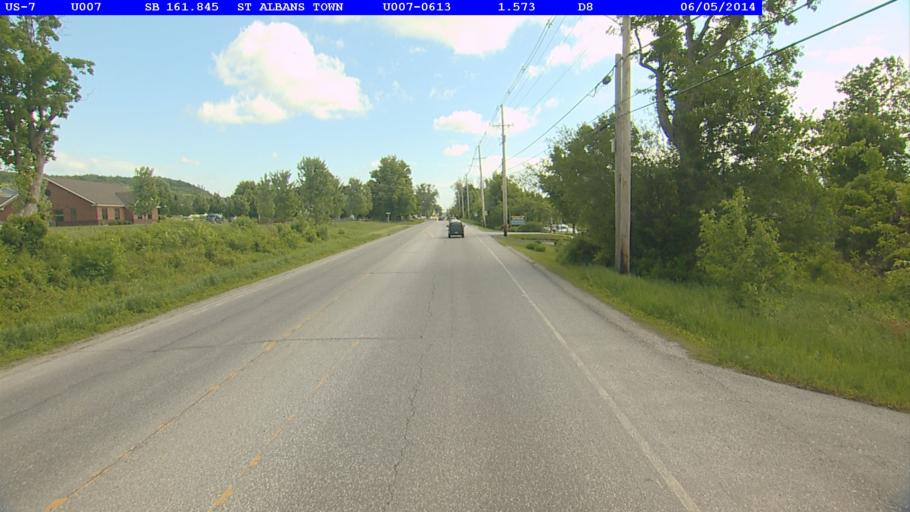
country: US
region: Vermont
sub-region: Franklin County
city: Saint Albans
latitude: 44.8314
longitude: -73.0795
